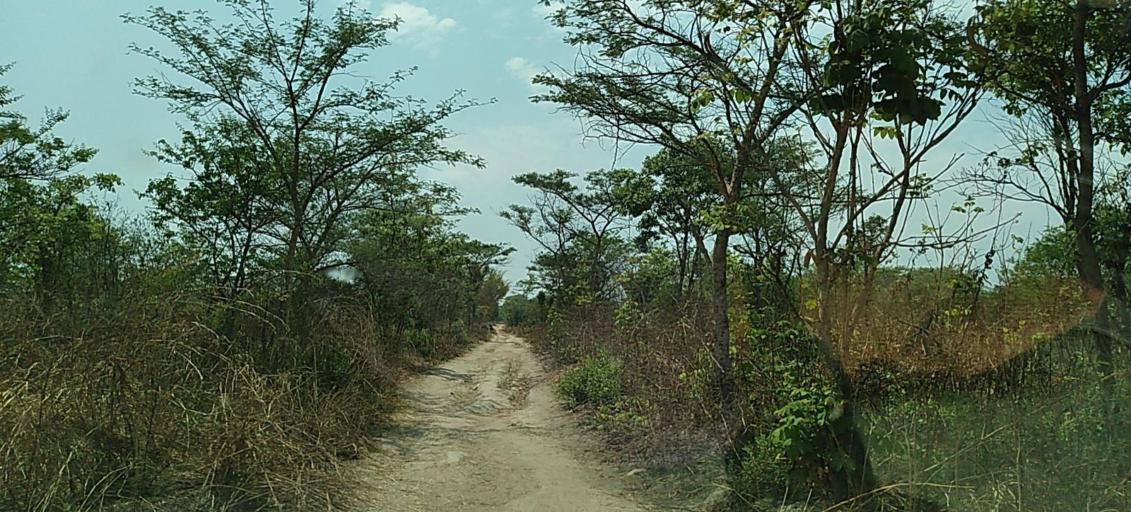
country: ZM
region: Copperbelt
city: Kalulushi
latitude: -12.9472
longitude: 28.1297
